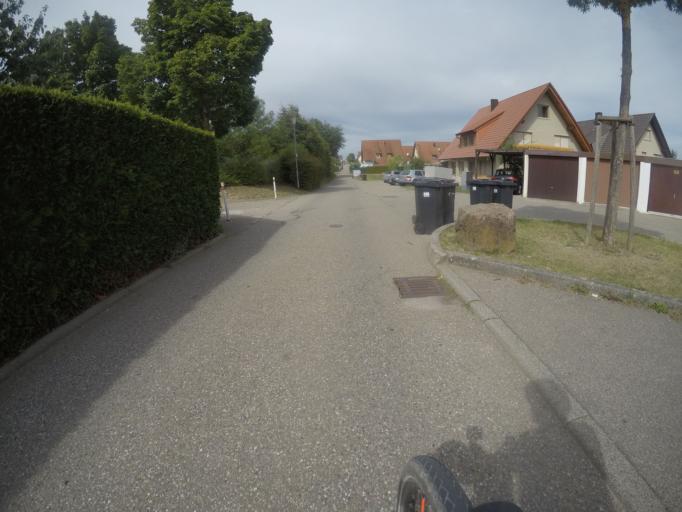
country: DE
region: Baden-Wuerttemberg
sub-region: Karlsruhe Region
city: Eutingen
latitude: 48.8821
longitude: 8.7631
